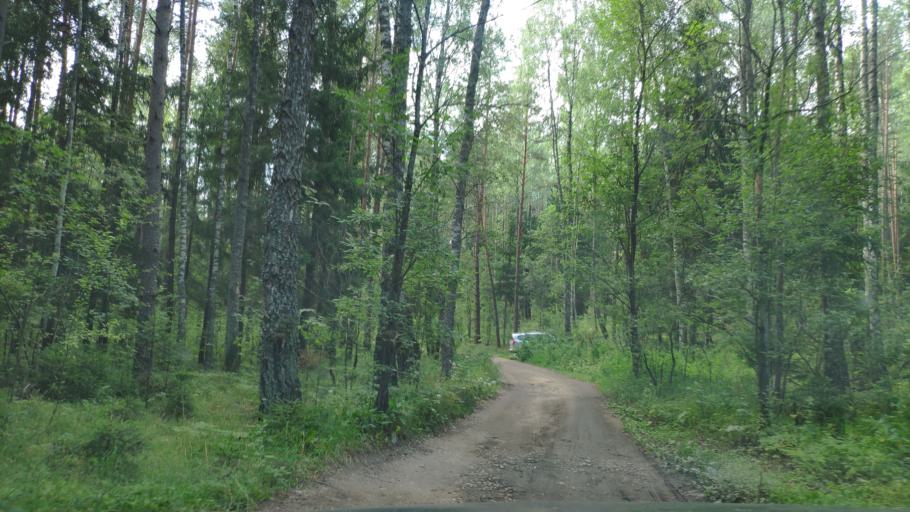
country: BY
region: Minsk
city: Khatsyezhyna
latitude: 53.9575
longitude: 27.3081
